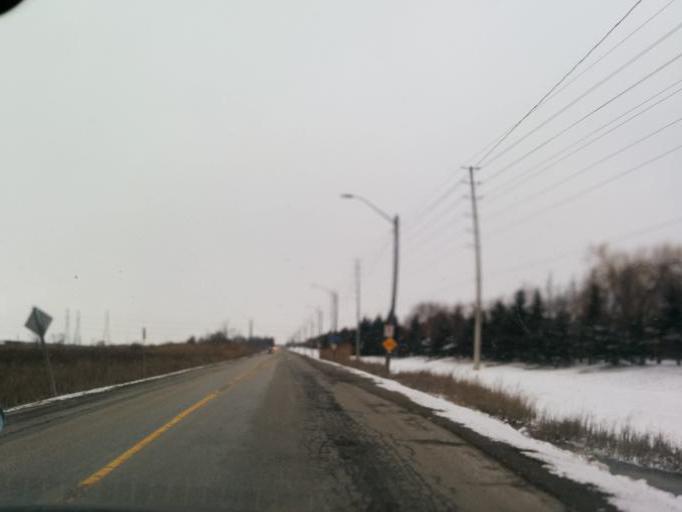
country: CA
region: Ontario
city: Brampton
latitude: 43.5758
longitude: -79.7890
